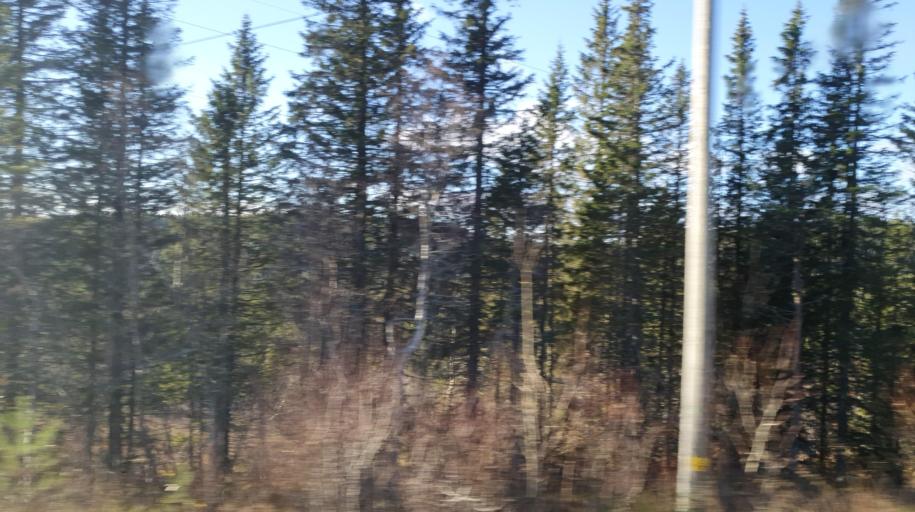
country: NO
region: Buskerud
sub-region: Krodsherad
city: Noresund
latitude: 60.2177
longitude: 9.5365
